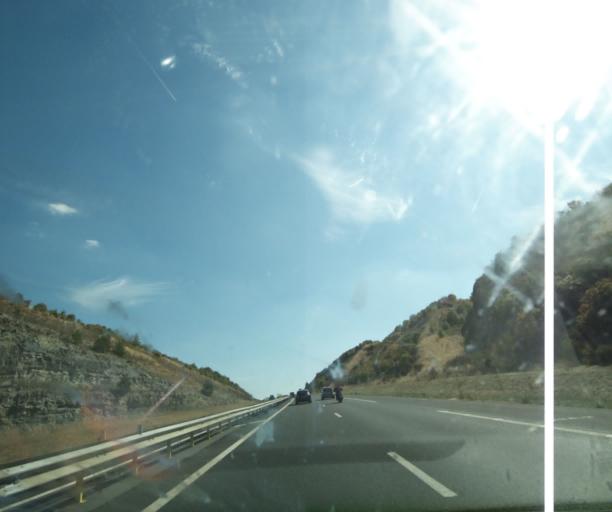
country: FR
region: Limousin
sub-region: Departement de la Correze
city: Brive-la-Gaillarde
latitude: 45.0580
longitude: 1.5074
